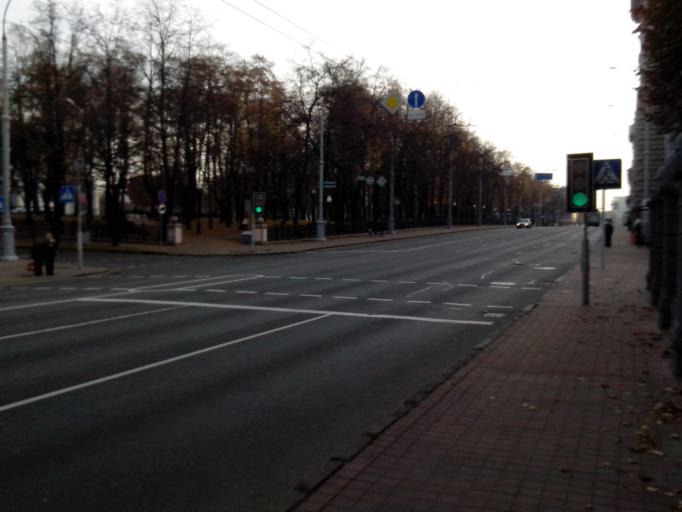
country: BY
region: Minsk
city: Minsk
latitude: 53.9120
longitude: 27.5599
